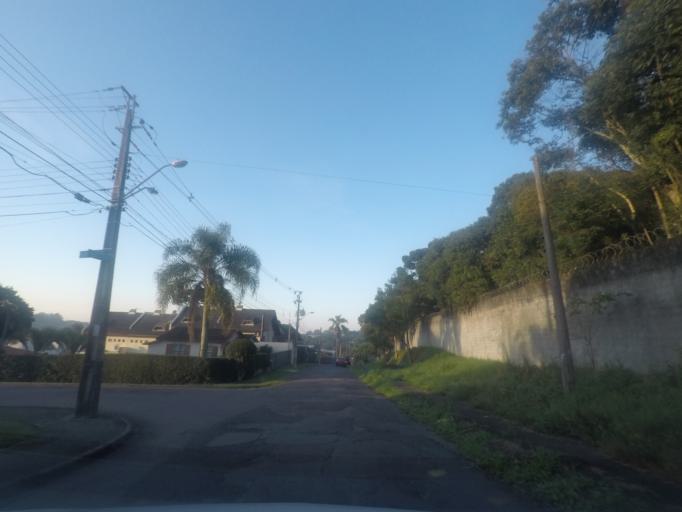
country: BR
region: Parana
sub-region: Curitiba
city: Curitiba
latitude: -25.3845
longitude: -49.2696
